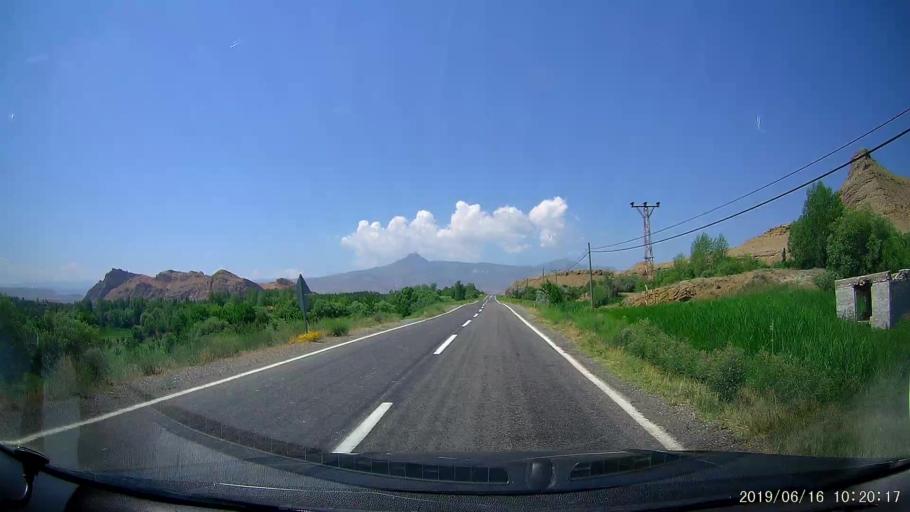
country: TR
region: Igdir
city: Tuzluca
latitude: 40.1492
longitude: 43.6493
